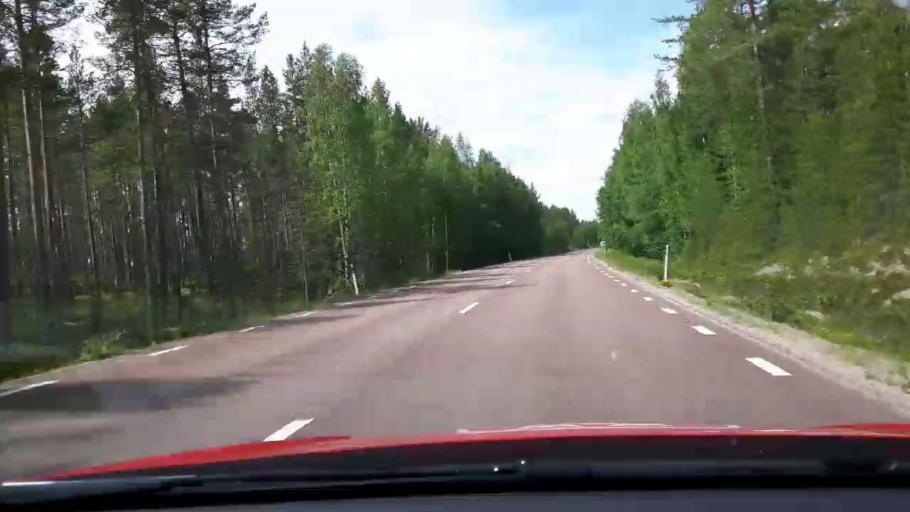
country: SE
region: Jaemtland
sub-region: Harjedalens Kommun
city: Sveg
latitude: 62.0449
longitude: 14.8563
